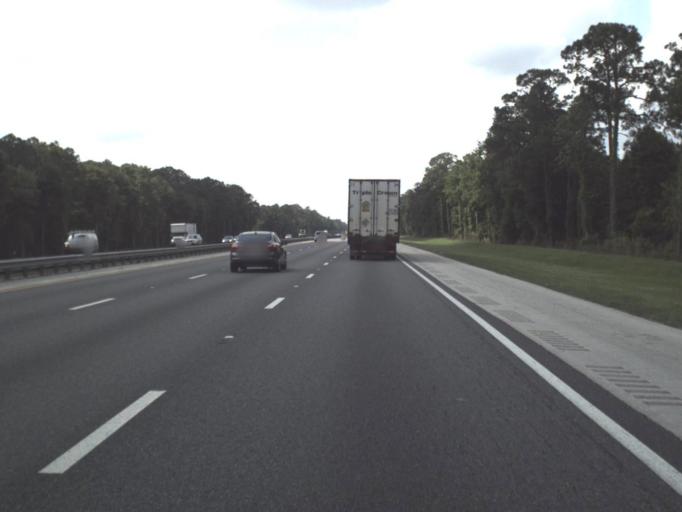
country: US
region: Florida
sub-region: Saint Johns County
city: Saint Augustine
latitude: 29.9413
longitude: -81.4305
